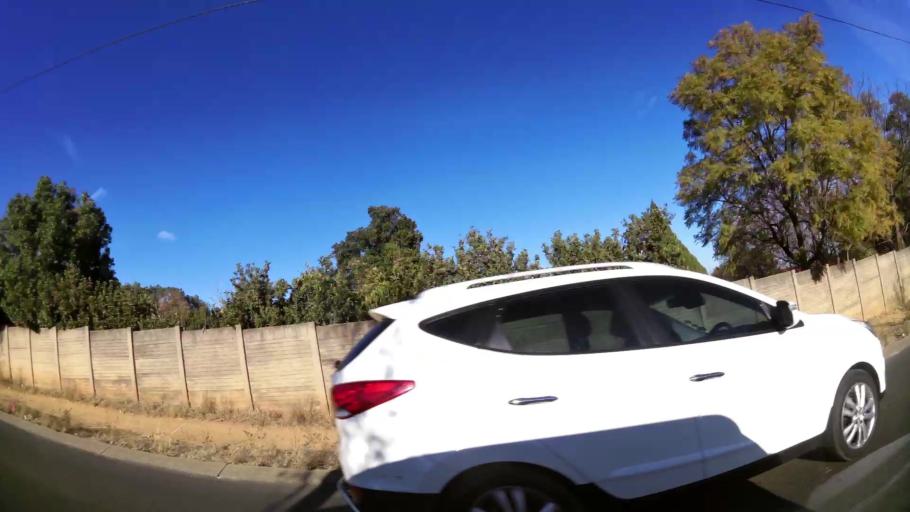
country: ZA
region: Gauteng
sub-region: City of Johannesburg Metropolitan Municipality
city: Midrand
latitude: -26.0210
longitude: 28.1446
